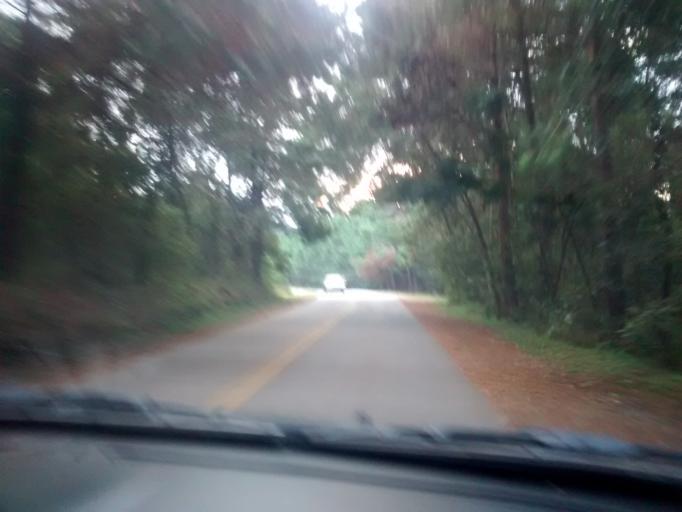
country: BR
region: Sao Paulo
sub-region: Campos Do Jordao
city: Campos do Jordao
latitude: -22.6482
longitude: -45.6237
